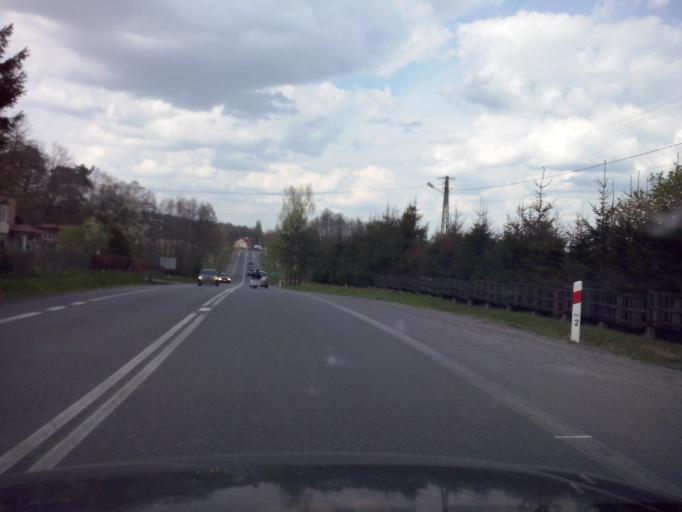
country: PL
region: Subcarpathian Voivodeship
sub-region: Powiat rzeszowski
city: Sokolow Malopolski
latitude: 50.2146
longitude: 22.1076
